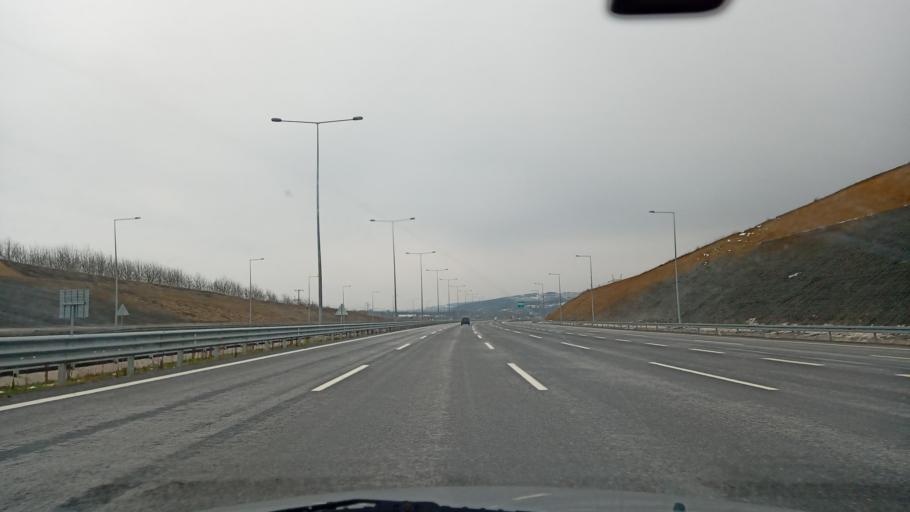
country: TR
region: Kocaeli
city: Akmese
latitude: 40.8441
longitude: 30.2154
